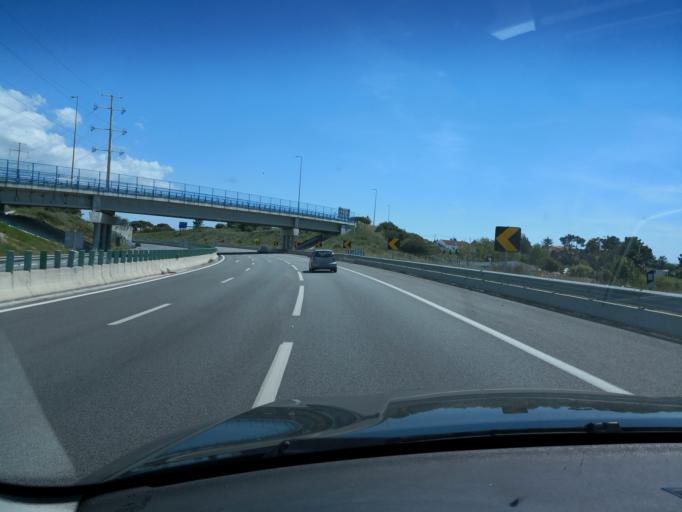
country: PT
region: Setubal
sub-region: Almada
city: Sobreda
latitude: 38.6414
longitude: -9.2018
